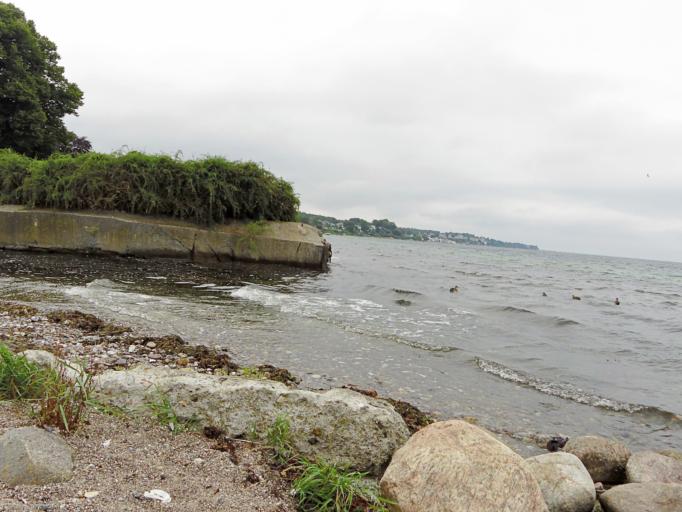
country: DK
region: Capital Region
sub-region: Rudersdal Kommune
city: Trorod
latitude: 55.8077
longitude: 12.5824
